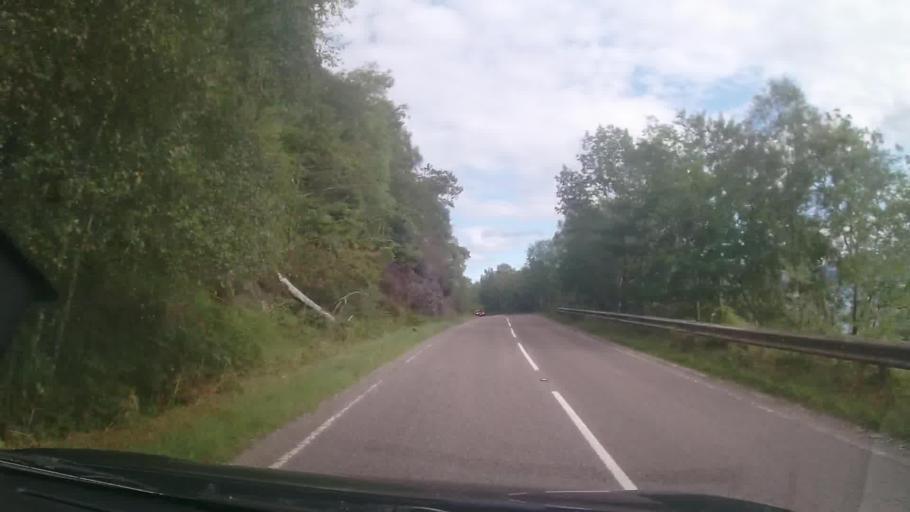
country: GB
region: Scotland
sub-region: Highland
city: Fort William
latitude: 56.7061
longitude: -5.3132
